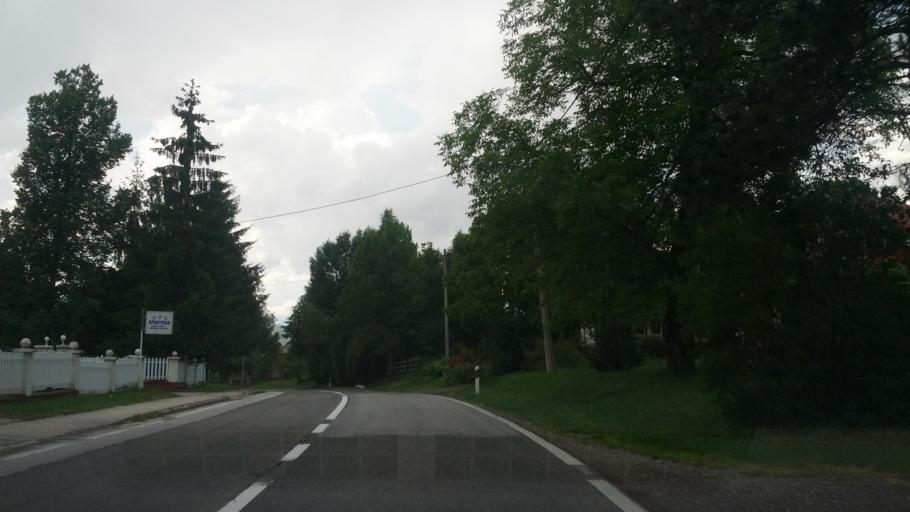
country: HR
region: Licko-Senjska
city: Jezerce
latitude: 44.9537
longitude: 15.6716
